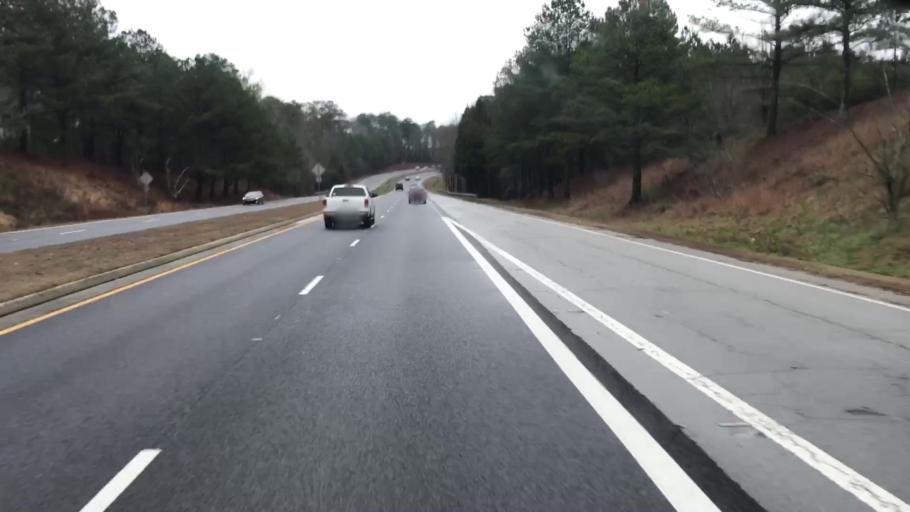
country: US
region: Georgia
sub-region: Gwinnett County
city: Snellville
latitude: 33.8900
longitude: -84.0507
